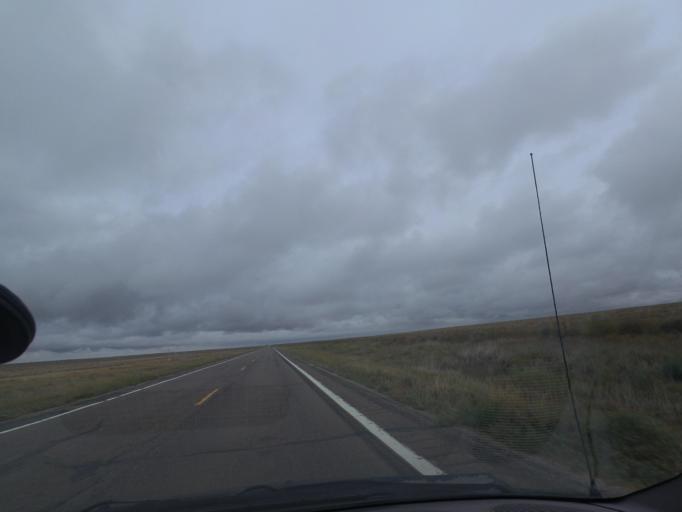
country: US
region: Colorado
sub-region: Washington County
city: Akron
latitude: 39.7274
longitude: -103.1293
